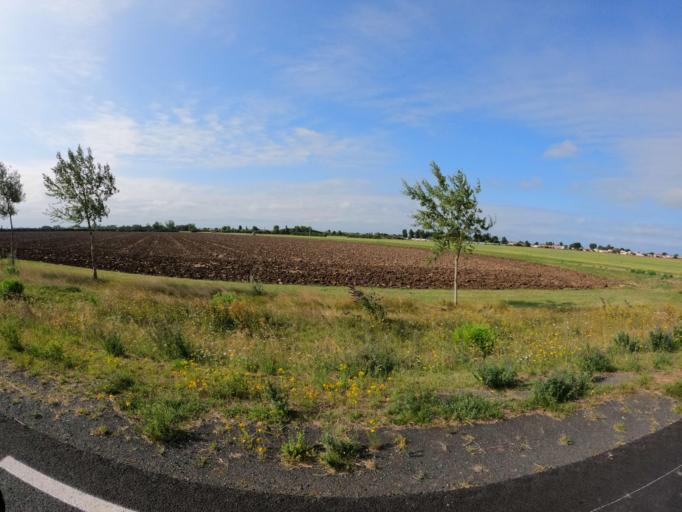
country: FR
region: Pays de la Loire
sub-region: Departement de la Vendee
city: Triaize
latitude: 46.3435
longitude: -1.3034
